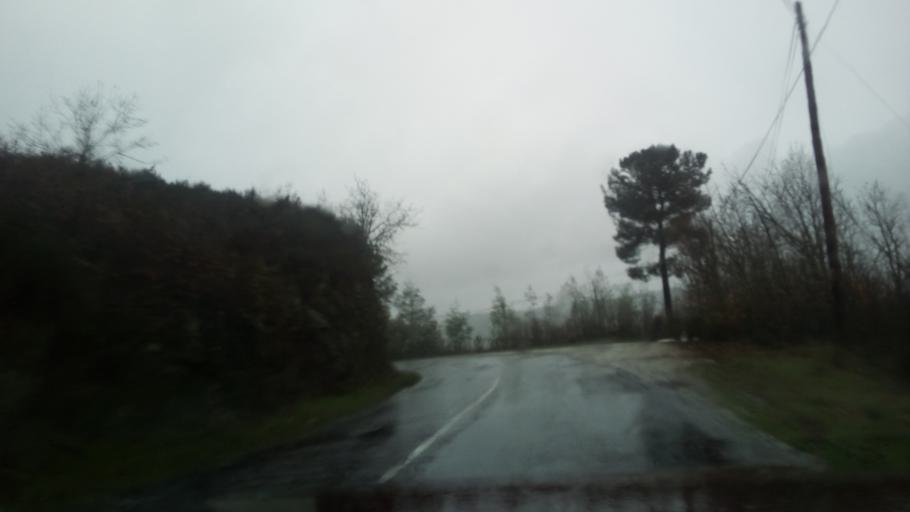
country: PT
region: Guarda
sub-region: Fornos de Algodres
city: Fornos de Algodres
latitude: 40.6276
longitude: -7.4666
